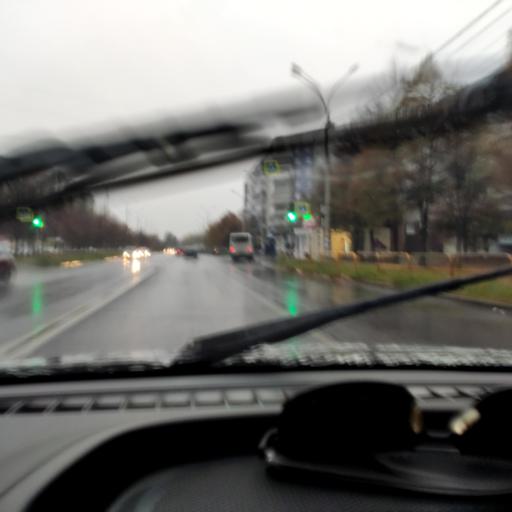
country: RU
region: Samara
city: Tol'yatti
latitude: 53.5391
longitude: 49.4014
